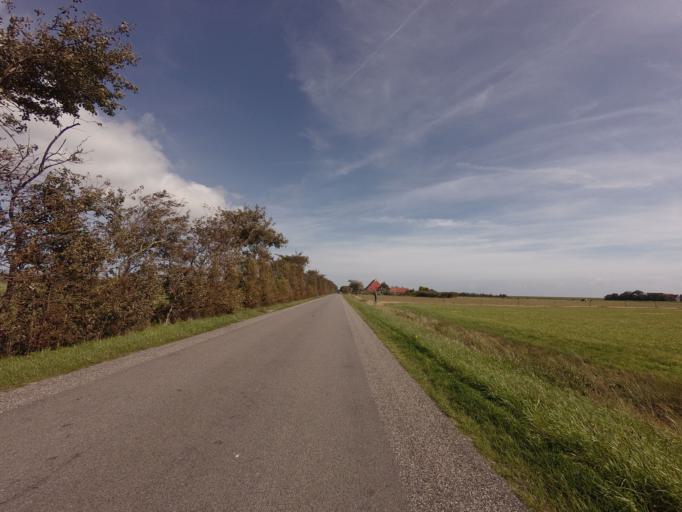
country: NL
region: Friesland
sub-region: Gemeente Ameland
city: Hollum
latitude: 53.4408
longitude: 5.7037
